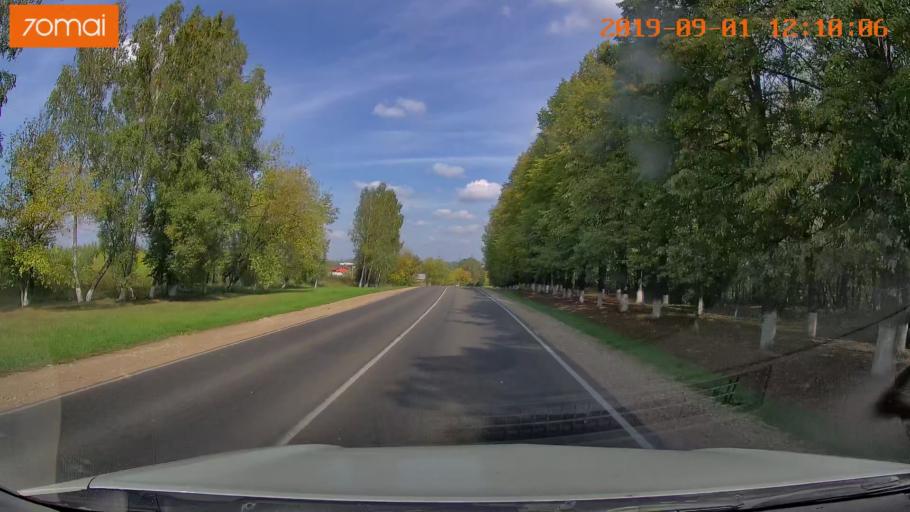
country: RU
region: Kaluga
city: Maloyaroslavets
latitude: 54.9878
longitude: 36.4305
